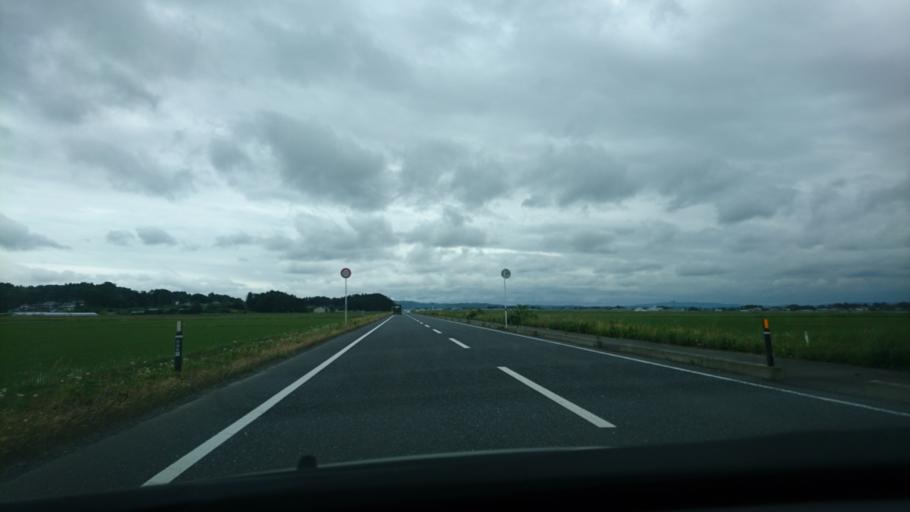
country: JP
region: Miyagi
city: Wakuya
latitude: 38.7033
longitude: 141.2601
